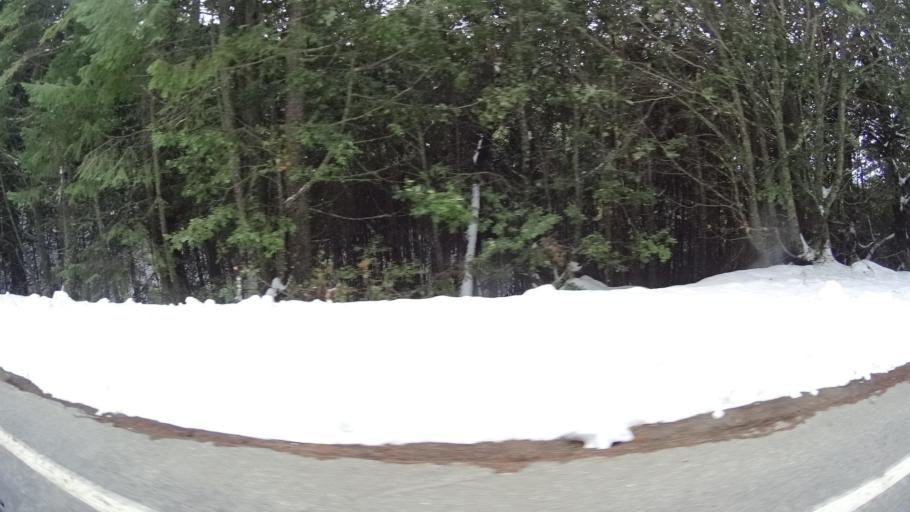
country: US
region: California
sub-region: Humboldt County
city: Willow Creek
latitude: 40.8669
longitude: -123.7419
